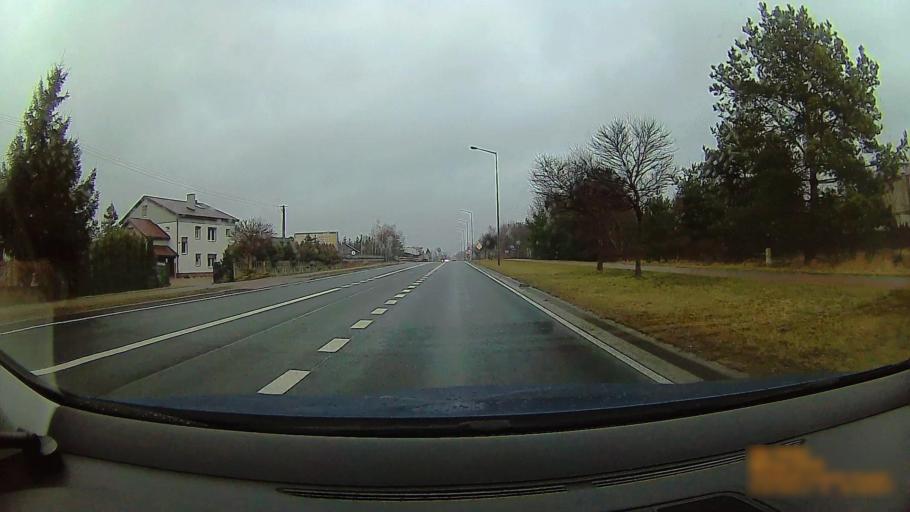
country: PL
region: Greater Poland Voivodeship
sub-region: Konin
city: Konin
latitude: 52.1780
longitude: 18.2710
